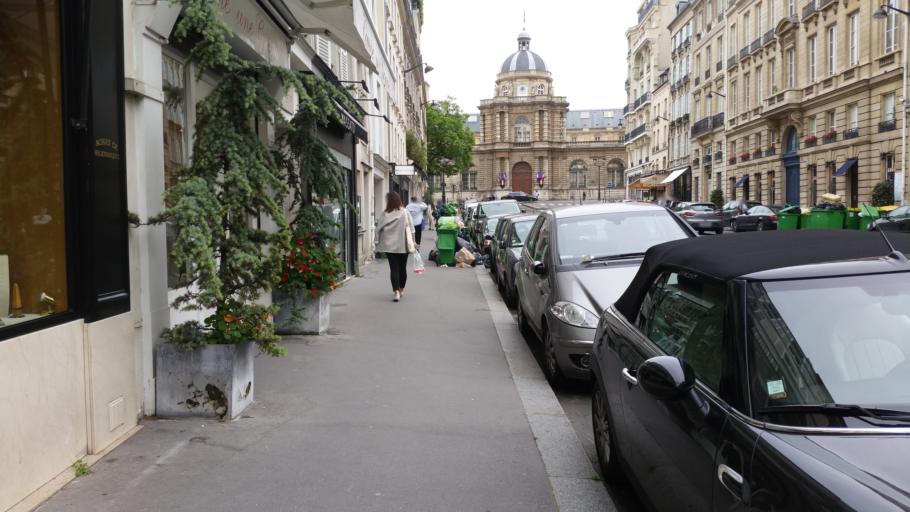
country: FR
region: Ile-de-France
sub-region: Paris
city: Paris
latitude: 48.8501
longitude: 2.3374
